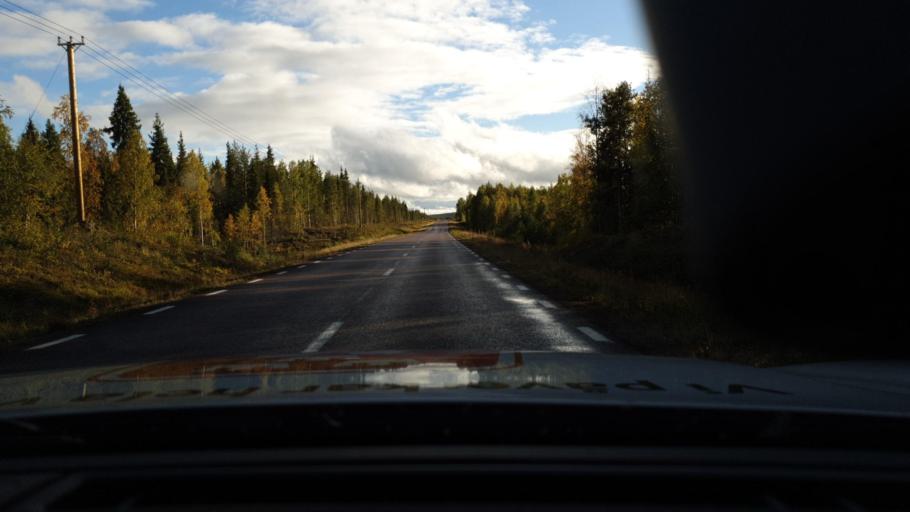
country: SE
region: Norrbotten
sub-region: Overkalix Kommun
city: OEverkalix
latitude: 66.8869
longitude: 22.7678
